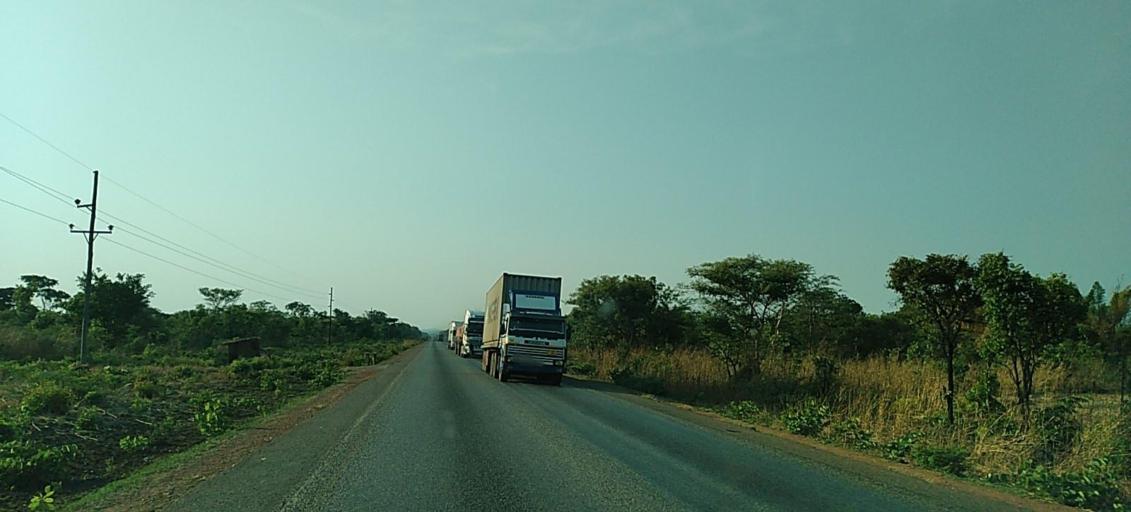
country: ZM
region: Copperbelt
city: Luanshya
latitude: -13.2655
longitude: 28.6786
